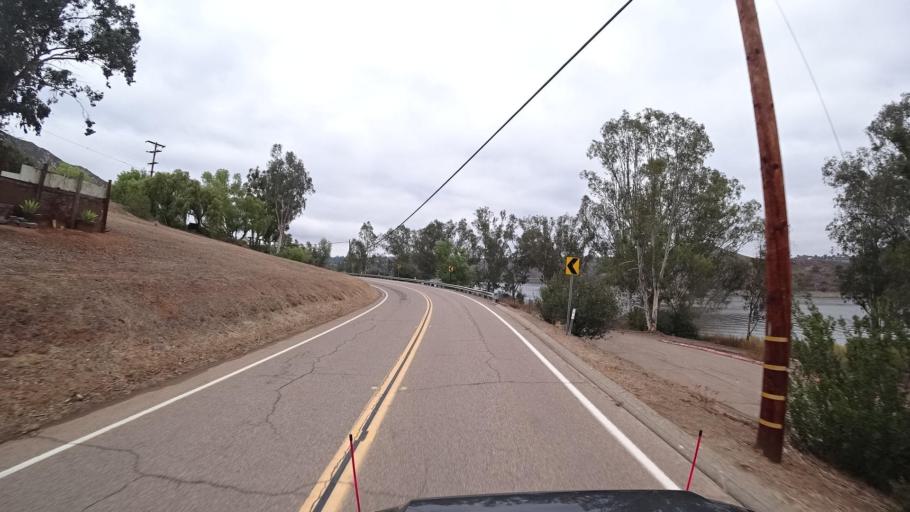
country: US
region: California
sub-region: San Diego County
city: Escondido
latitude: 33.0636
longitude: -117.1195
